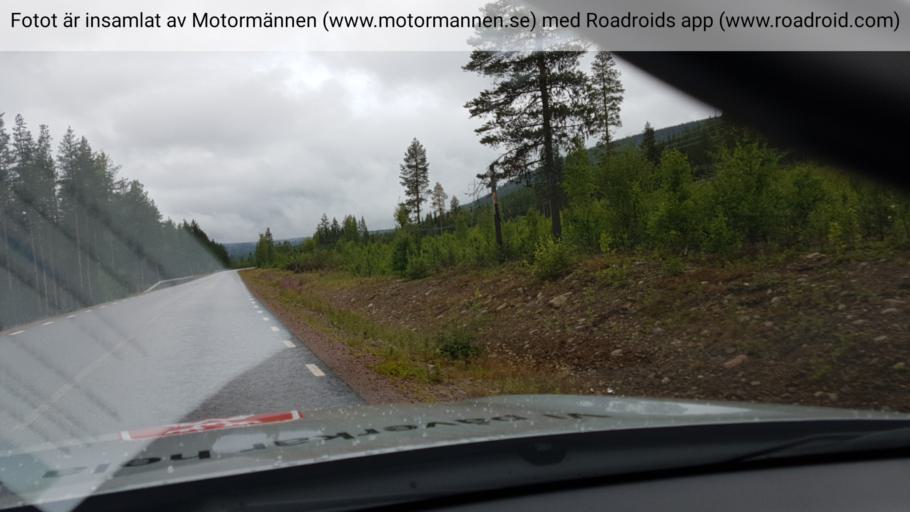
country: SE
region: Norrbotten
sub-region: Gallivare Kommun
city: Gaellivare
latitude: 66.6551
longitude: 20.3774
